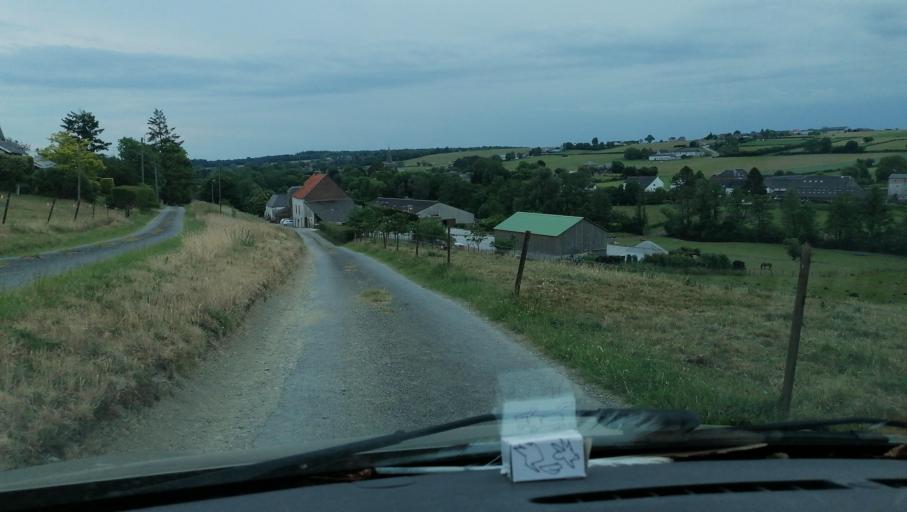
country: BE
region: Wallonia
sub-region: Province du Hainaut
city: Beaumont
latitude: 50.2040
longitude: 4.1657
